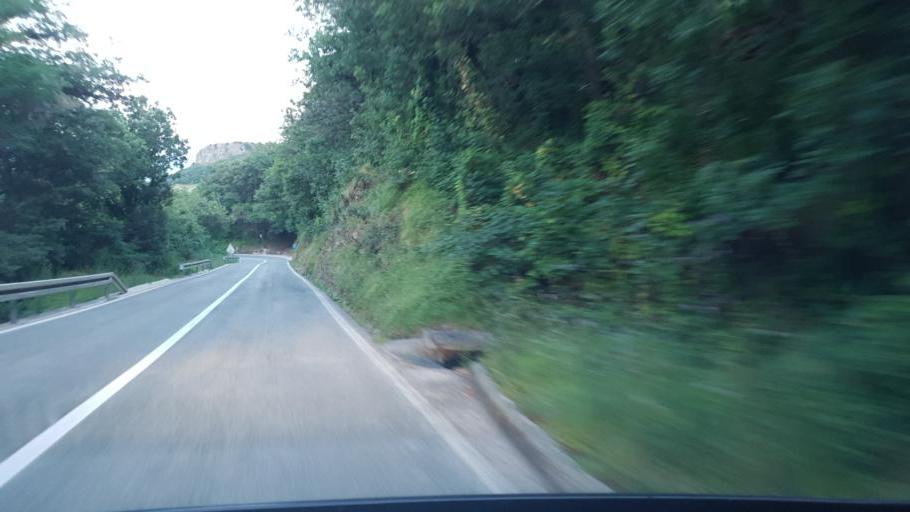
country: HR
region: Primorsko-Goranska
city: Punat
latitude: 45.0230
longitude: 14.6810
